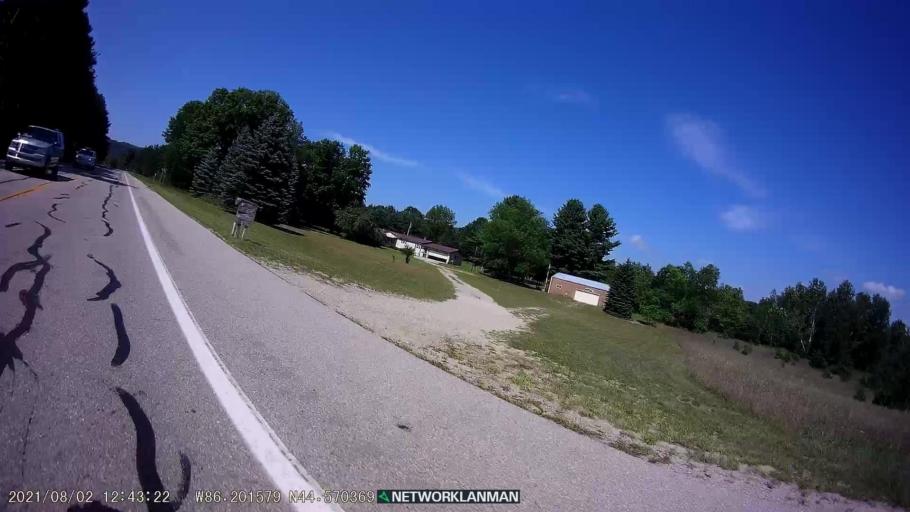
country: US
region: Michigan
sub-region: Benzie County
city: Frankfort
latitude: 44.5707
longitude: -86.2018
